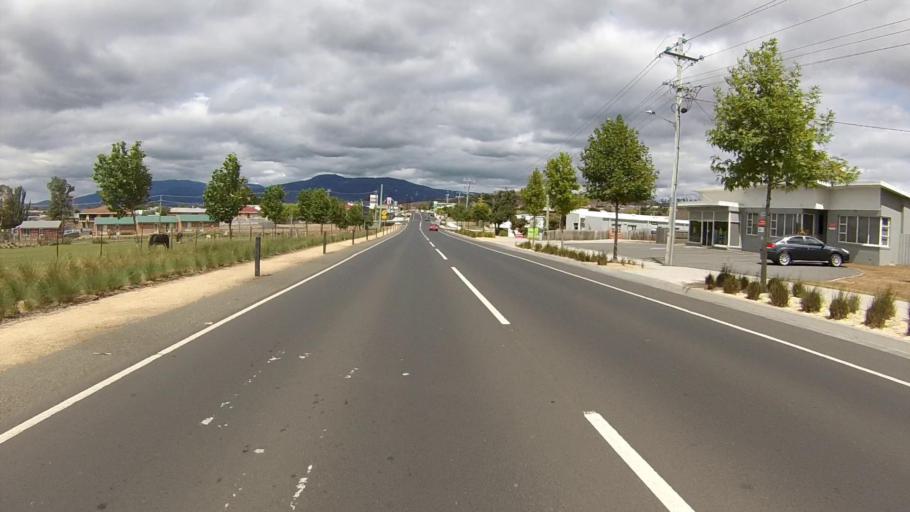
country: AU
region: Tasmania
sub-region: Brighton
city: Bridgewater
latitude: -42.6960
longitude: 147.2548
